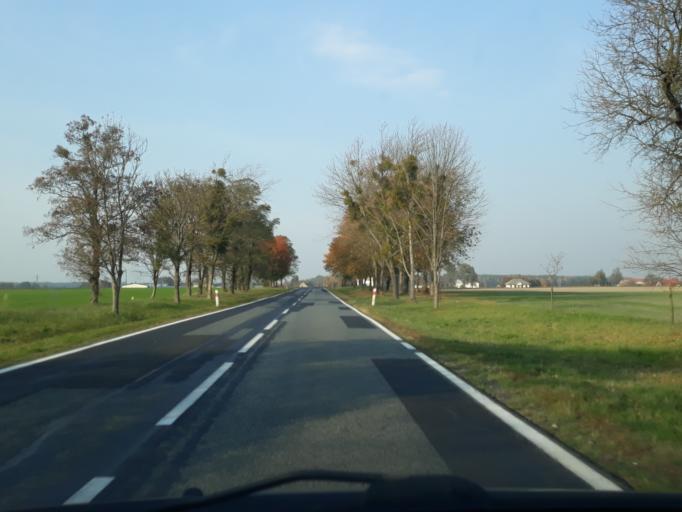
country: PL
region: Kujawsko-Pomorskie
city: Kamien Krajenski
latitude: 53.5794
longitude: 17.4939
